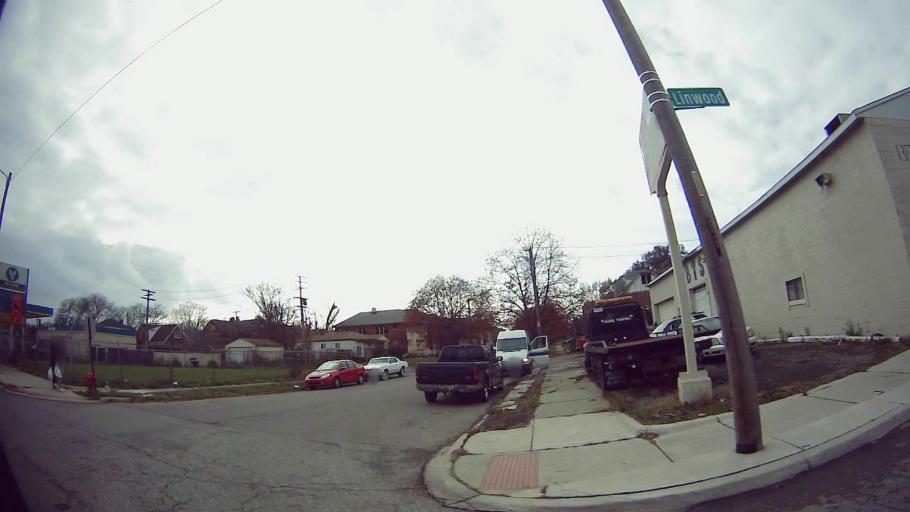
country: US
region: Michigan
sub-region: Wayne County
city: Highland Park
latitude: 42.3894
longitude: -83.1197
